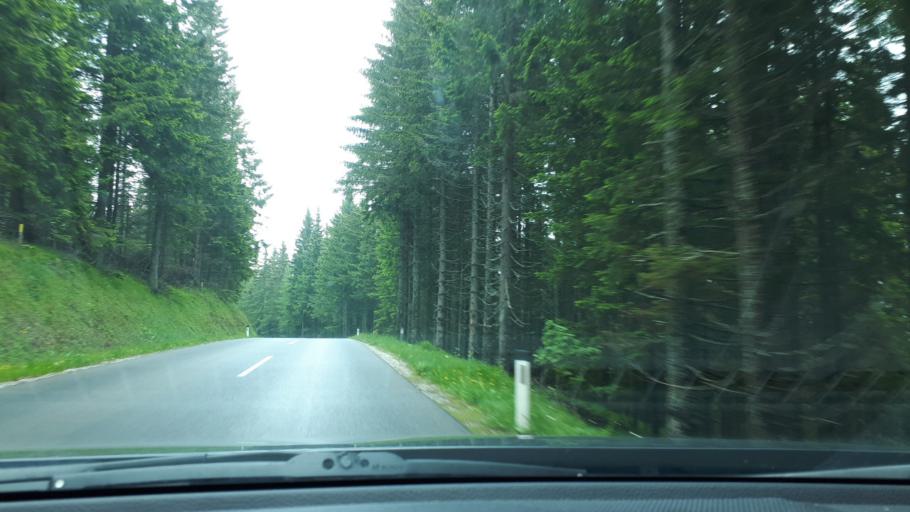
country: AT
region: Styria
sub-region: Politischer Bezirk Voitsberg
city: Modriach
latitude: 46.9196
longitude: 15.0225
